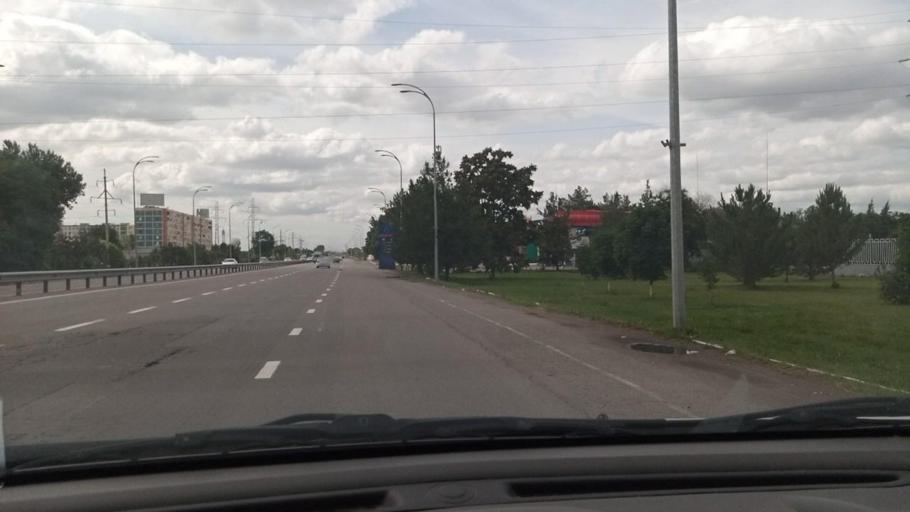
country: UZ
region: Toshkent Shahri
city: Bektemir
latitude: 41.2538
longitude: 69.3847
